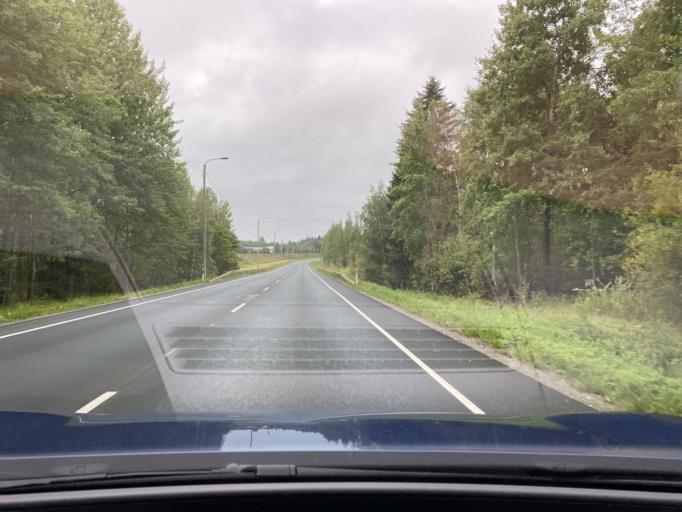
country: FI
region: Kymenlaakso
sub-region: Kouvola
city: Kouvola
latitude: 60.8910
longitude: 26.6044
